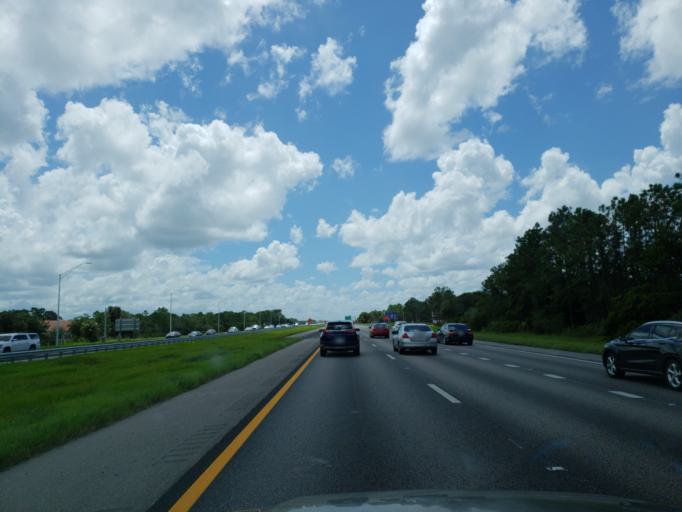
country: US
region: Florida
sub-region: Sarasota County
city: The Meadows
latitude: 27.4041
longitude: -82.4507
